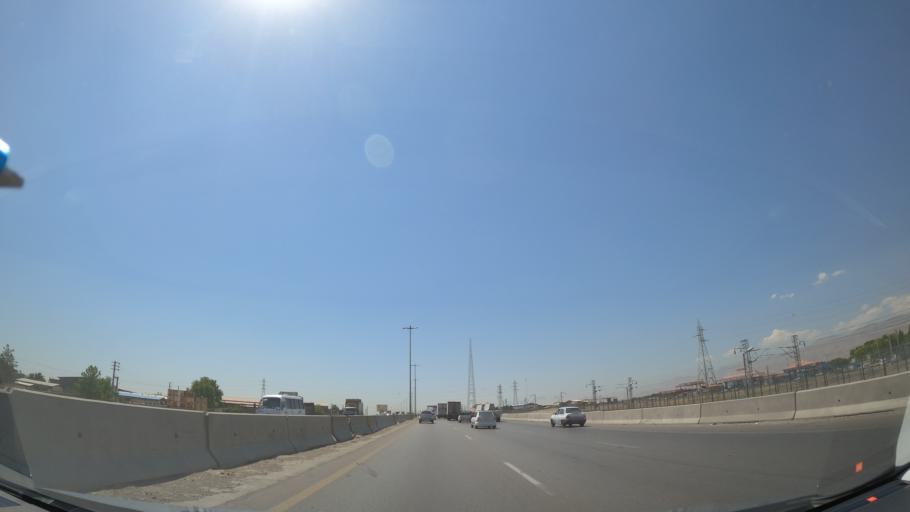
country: IR
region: Alborz
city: Hashtgerd
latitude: 35.9110
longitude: 50.8315
